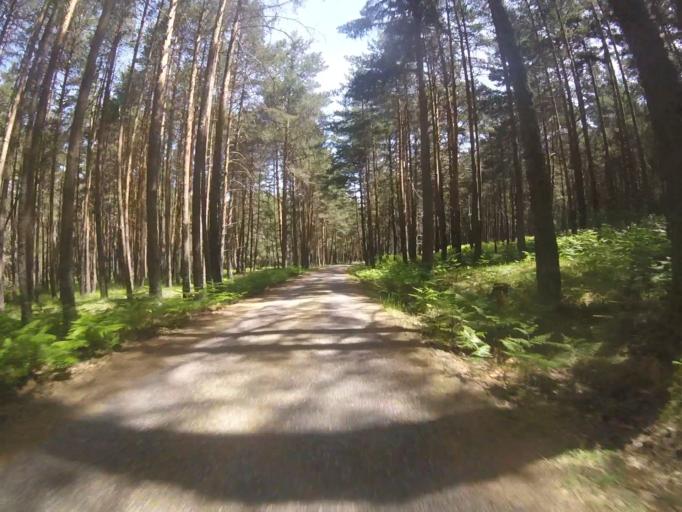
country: ES
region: Madrid
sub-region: Provincia de Madrid
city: Cercedilla
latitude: 40.8118
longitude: -4.0328
